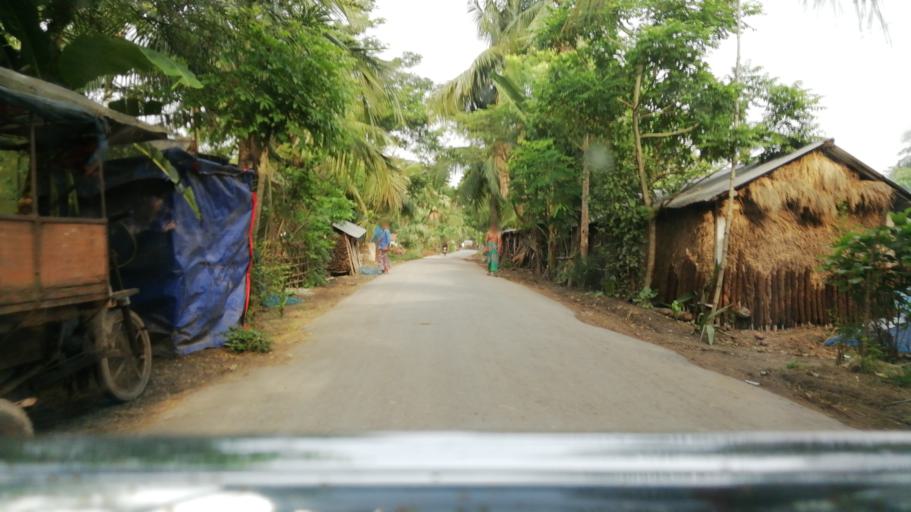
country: BD
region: Khulna
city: Bhatpara Abhaynagar
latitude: 23.0362
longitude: 89.2992
